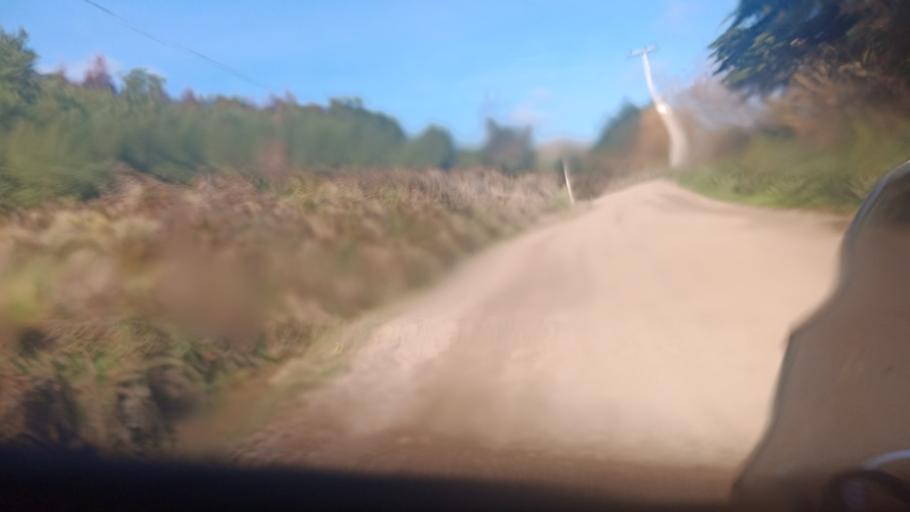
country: NZ
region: Bay of Plenty
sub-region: Opotiki District
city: Opotiki
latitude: -38.4195
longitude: 177.5581
